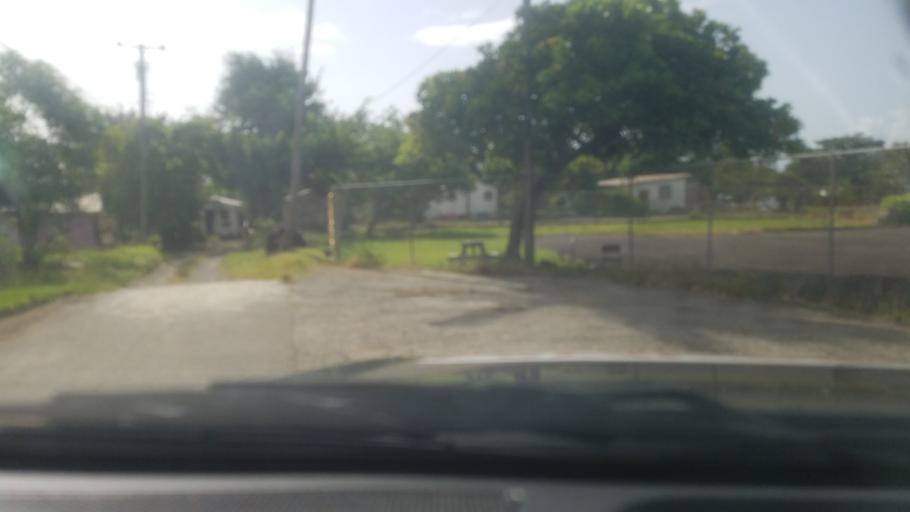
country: LC
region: Micoud Quarter
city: Micoud
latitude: 13.7974
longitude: -60.9198
